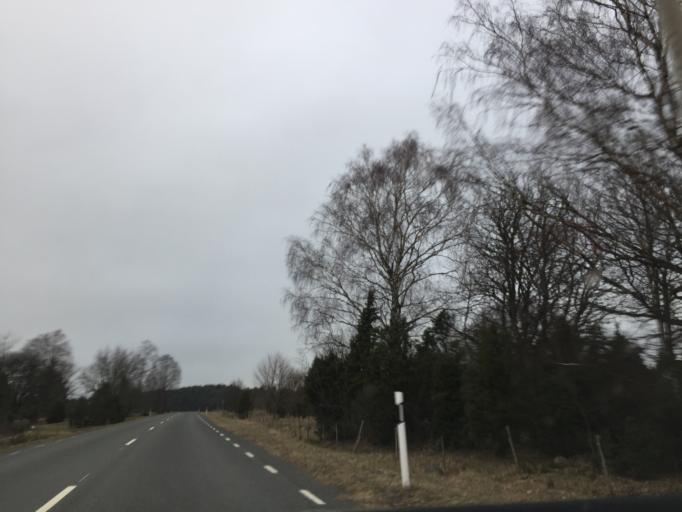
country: EE
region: Saare
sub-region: Kuressaare linn
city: Kuressaare
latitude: 58.5398
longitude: 22.3378
